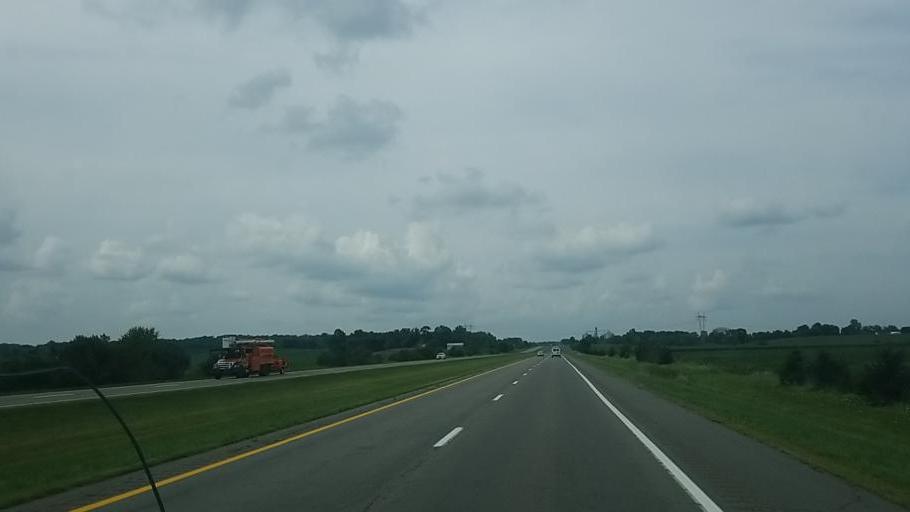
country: US
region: Ohio
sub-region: Knox County
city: Fredericktown
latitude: 40.4984
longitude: -82.5558
